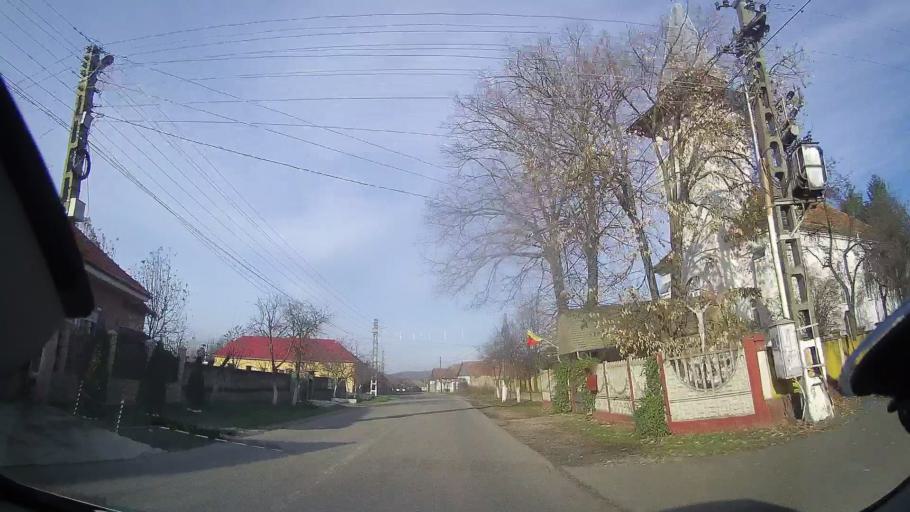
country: RO
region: Bihor
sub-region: Comuna Spinus
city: Spinus
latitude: 47.1741
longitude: 22.2181
